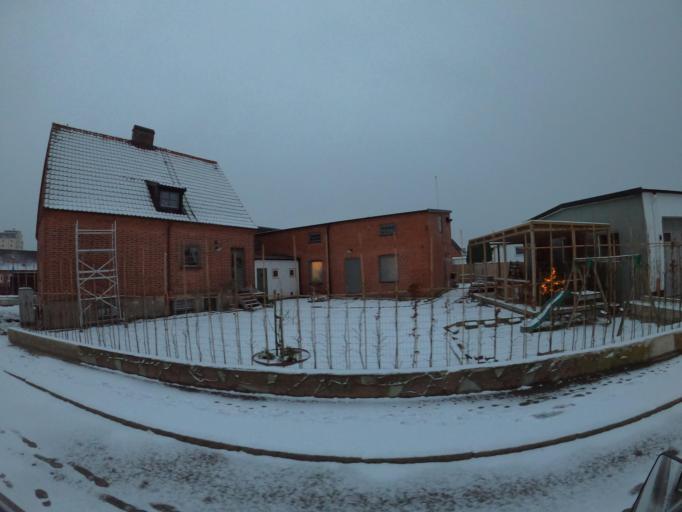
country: SE
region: Skane
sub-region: Svedala Kommun
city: Svedala
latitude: 55.5094
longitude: 13.2425
